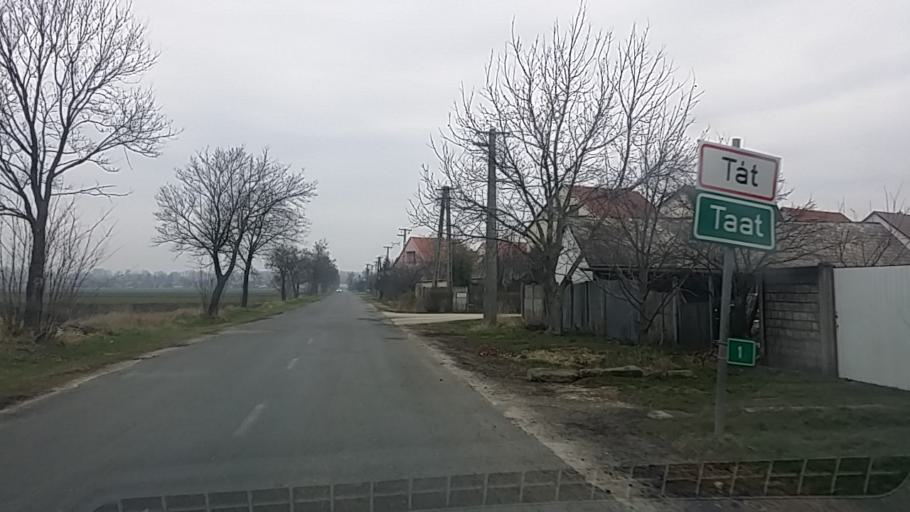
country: HU
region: Komarom-Esztergom
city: Tat
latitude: 47.7379
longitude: 18.6355
